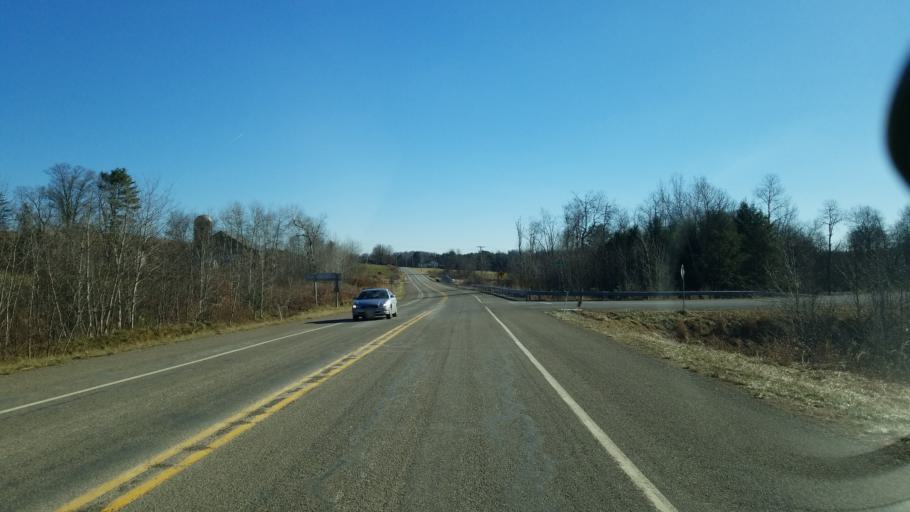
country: US
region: Pennsylvania
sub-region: Jefferson County
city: Falls Creek
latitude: 41.1856
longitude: -78.8783
